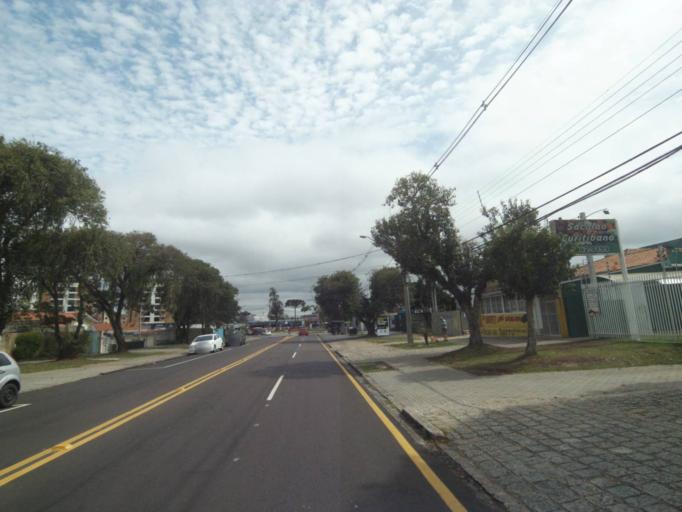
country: BR
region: Parana
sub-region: Curitiba
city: Curitiba
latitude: -25.4375
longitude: -49.2350
